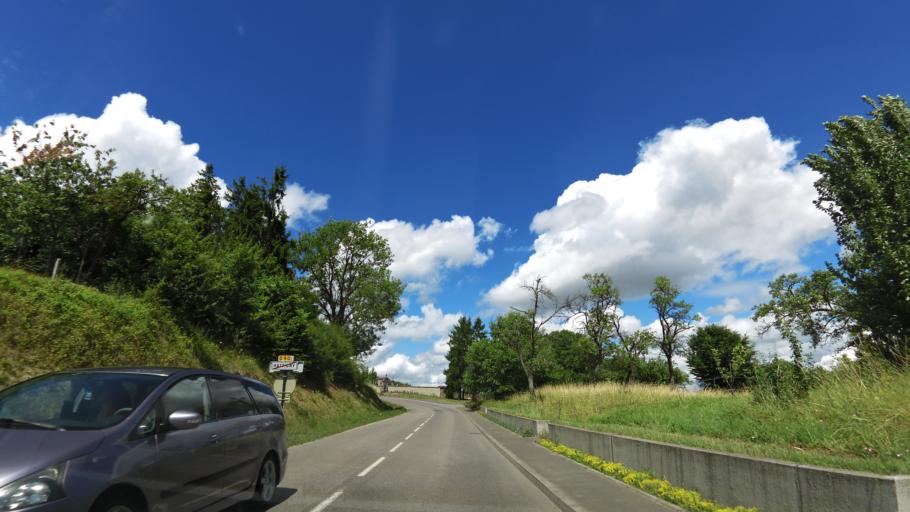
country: FR
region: Lorraine
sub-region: Departement de la Moselle
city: Lorquin
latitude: 48.6323
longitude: 6.9633
